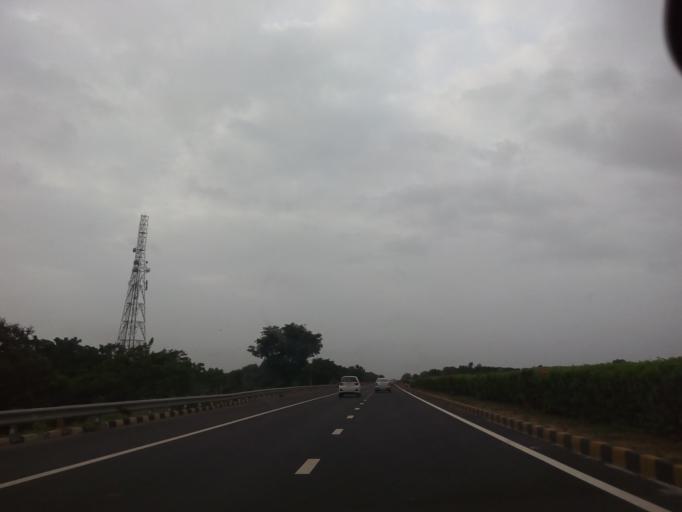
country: IN
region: Gujarat
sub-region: Kheda
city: Nadiad
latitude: 22.6887
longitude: 72.9037
